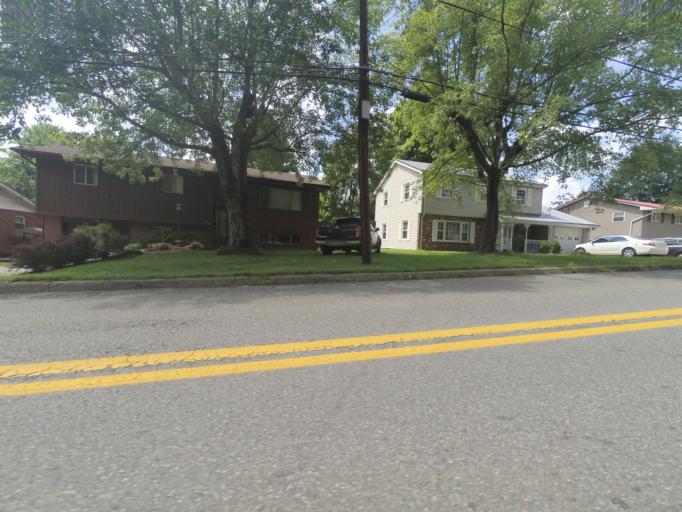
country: US
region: West Virginia
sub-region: Cabell County
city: Pea Ridge
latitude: 38.4030
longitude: -82.3803
